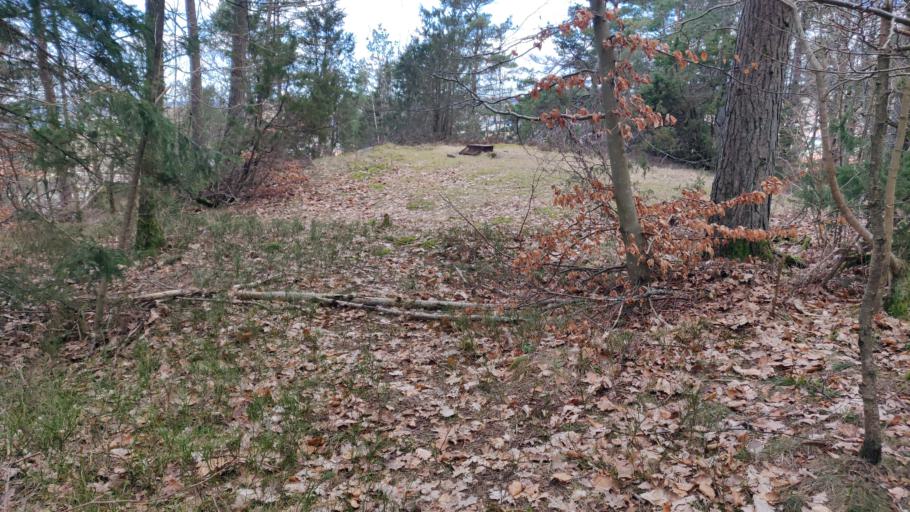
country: SE
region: Vaestra Goetaland
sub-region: Uddevalla Kommun
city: Uddevalla
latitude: 58.3418
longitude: 11.9337
